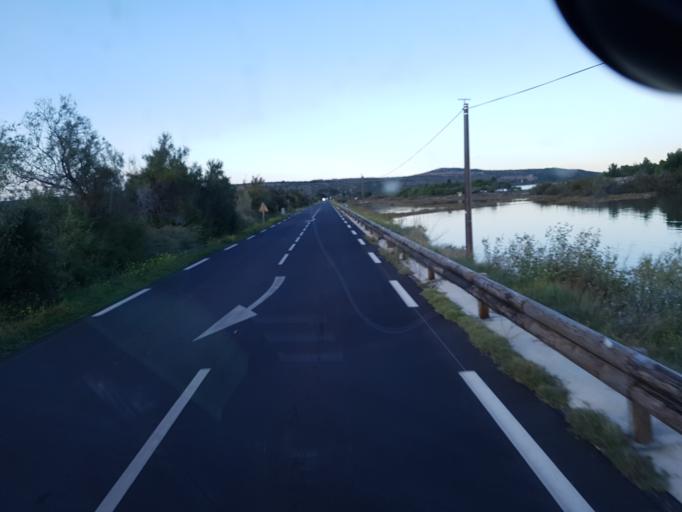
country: FR
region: Languedoc-Roussillon
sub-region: Departement de l'Aude
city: Leucate
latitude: 42.9660
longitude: 2.9975
